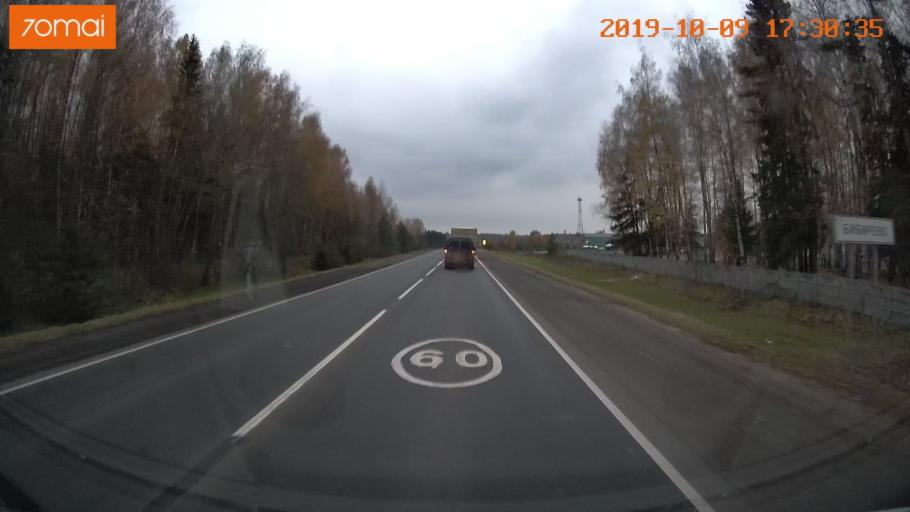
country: RU
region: Ivanovo
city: Bogorodskoye
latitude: 57.1418
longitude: 41.0482
